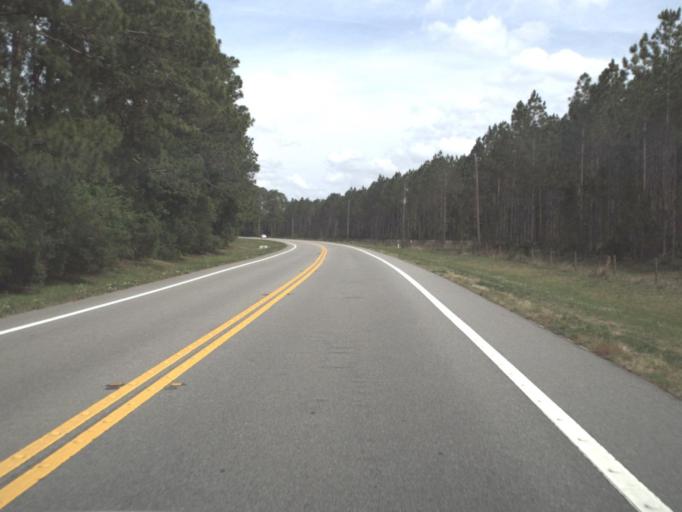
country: US
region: Florida
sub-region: Putnam County
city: Crescent City
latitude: 29.4814
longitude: -81.4523
